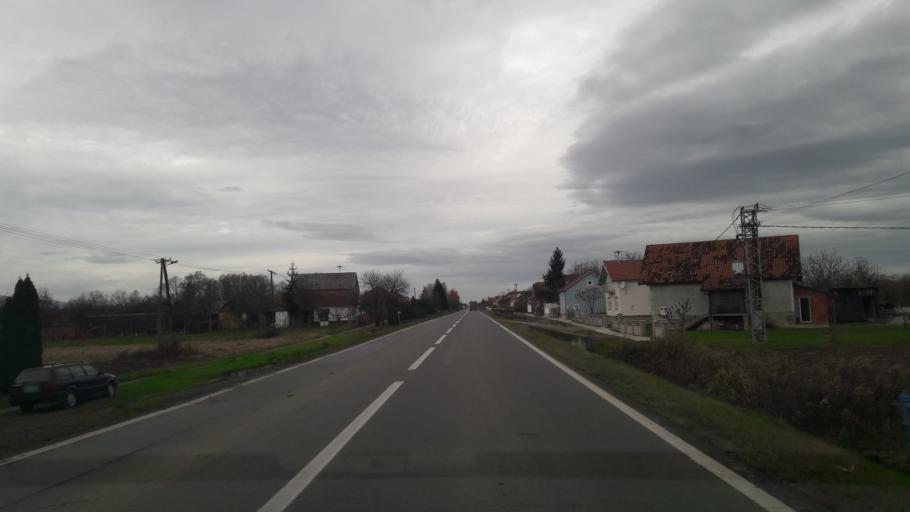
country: HR
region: Osjecko-Baranjska
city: Fericanci
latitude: 45.5273
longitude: 17.9592
